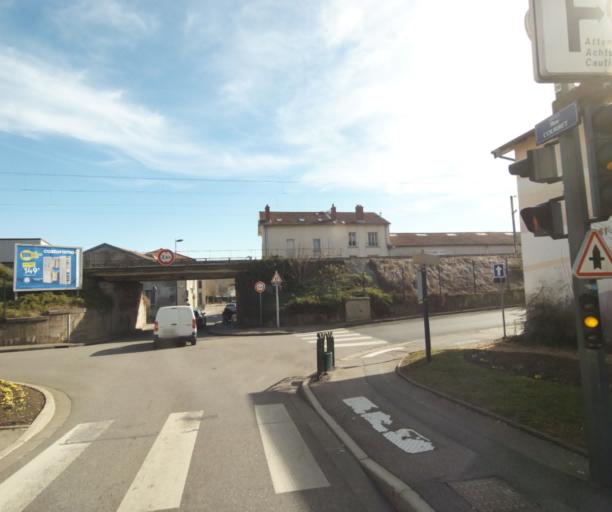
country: FR
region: Lorraine
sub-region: Departement de Meurthe-et-Moselle
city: Maxeville
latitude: 48.7129
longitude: 6.1668
